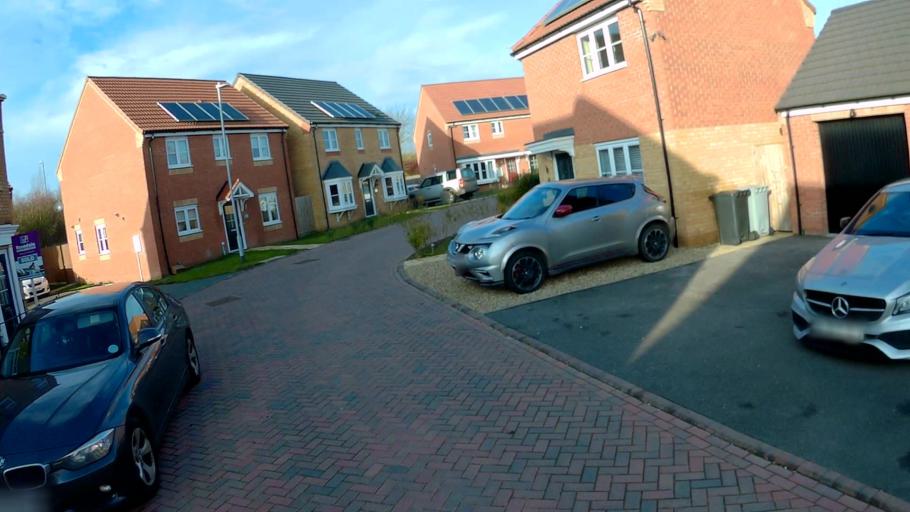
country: GB
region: England
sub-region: Lincolnshire
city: Bourne
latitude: 52.7647
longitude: -0.3951
